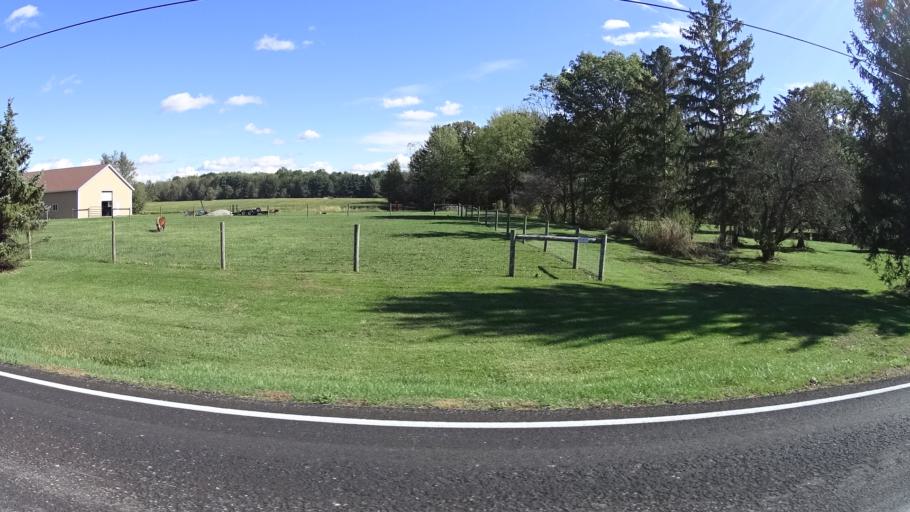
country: US
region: Ohio
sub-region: Lorain County
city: Grafton
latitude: 41.2708
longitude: -82.0791
